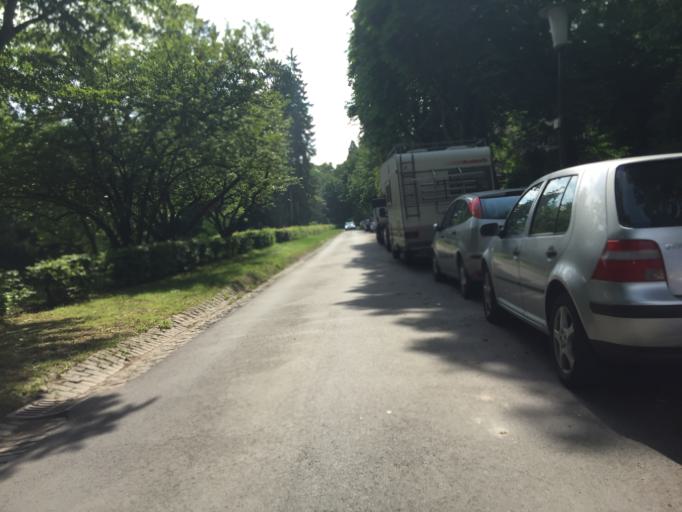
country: DE
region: Hesse
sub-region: Regierungsbezirk Darmstadt
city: Wiesbaden
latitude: 50.0940
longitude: 8.2292
